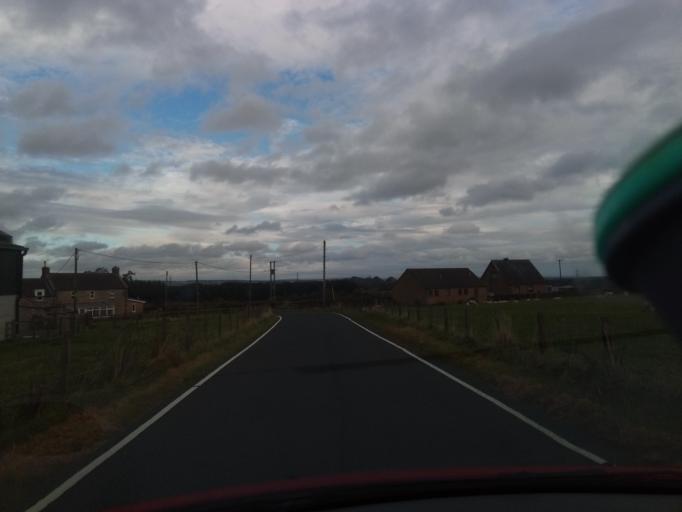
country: GB
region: Scotland
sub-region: West Lothian
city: Blackburn
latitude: 55.8301
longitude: -3.6090
